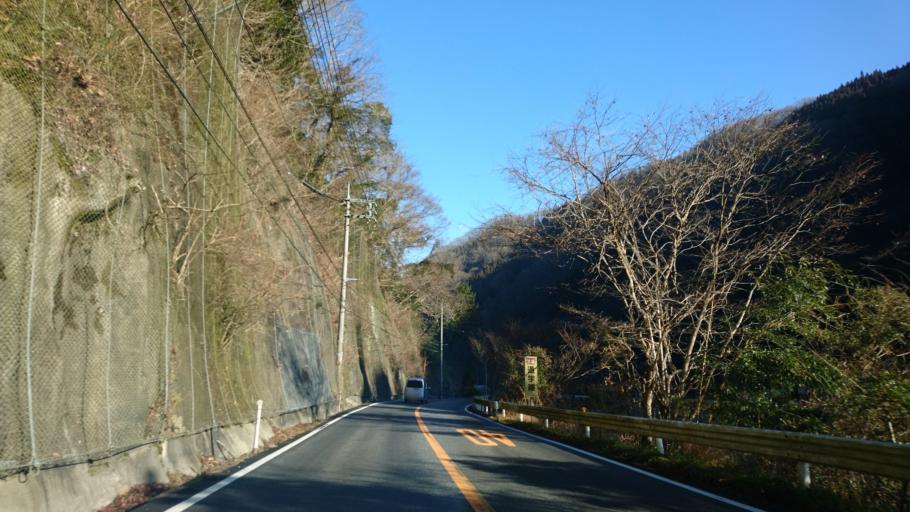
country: JP
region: Okayama
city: Takahashi
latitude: 34.8225
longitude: 133.6321
